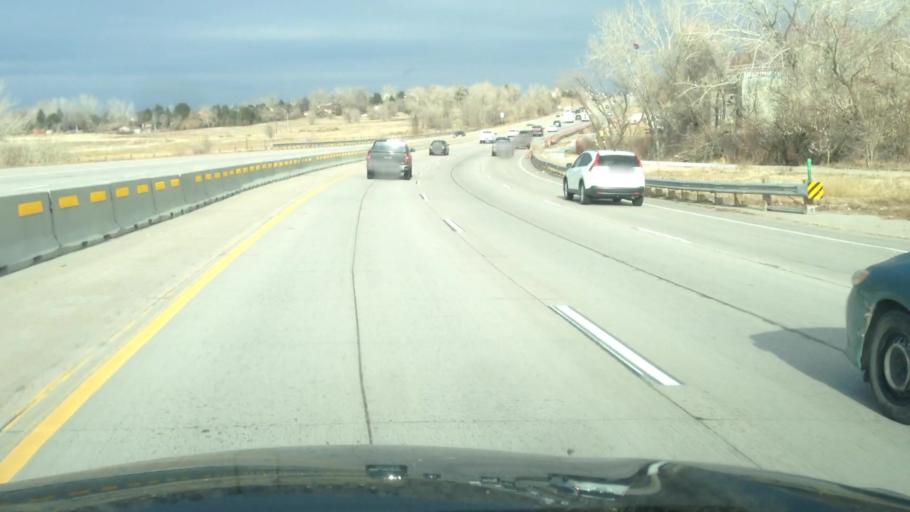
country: US
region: Colorado
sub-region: Arapahoe County
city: Dove Valley
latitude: 39.6178
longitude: -104.8191
